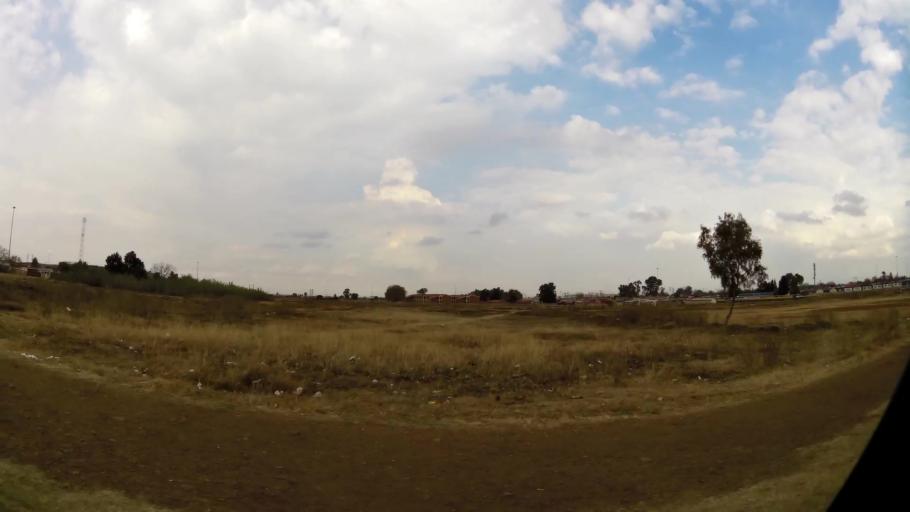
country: ZA
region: Gauteng
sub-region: Sedibeng District Municipality
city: Vanderbijlpark
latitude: -26.6697
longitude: 27.8490
